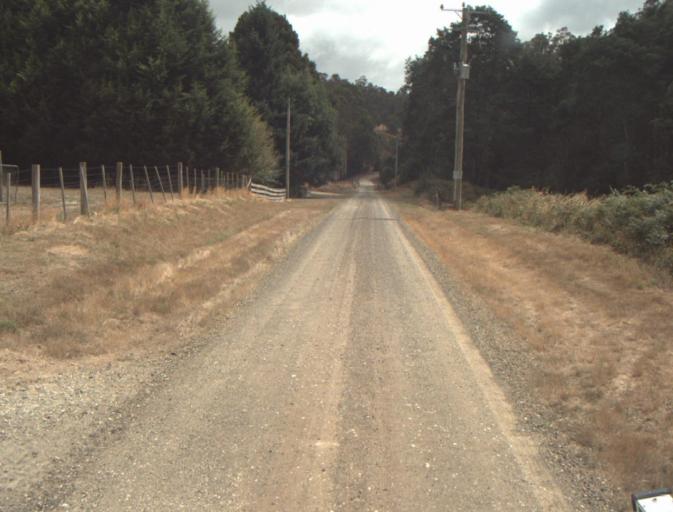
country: AU
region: Tasmania
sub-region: Dorset
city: Bridport
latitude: -41.1823
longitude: 147.2616
